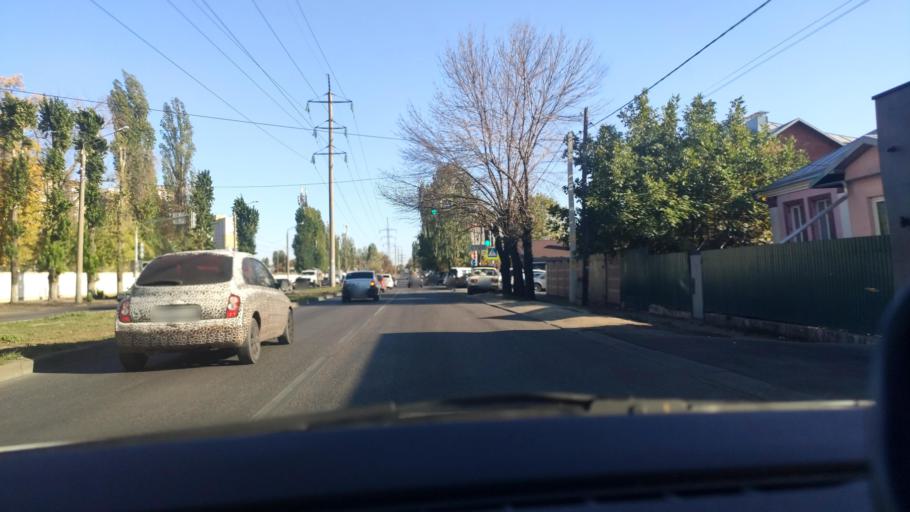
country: RU
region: Voronezj
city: Voronezh
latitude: 51.6347
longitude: 39.1745
